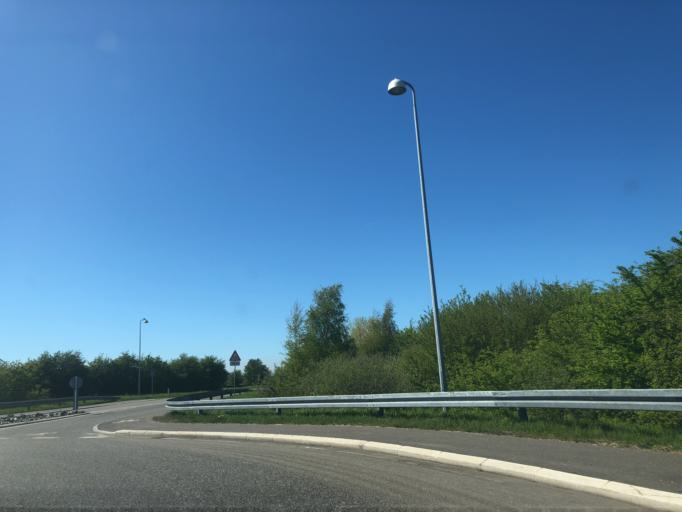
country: DK
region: Zealand
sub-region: Stevns Kommune
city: Store Heddinge
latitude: 55.3022
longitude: 12.3769
